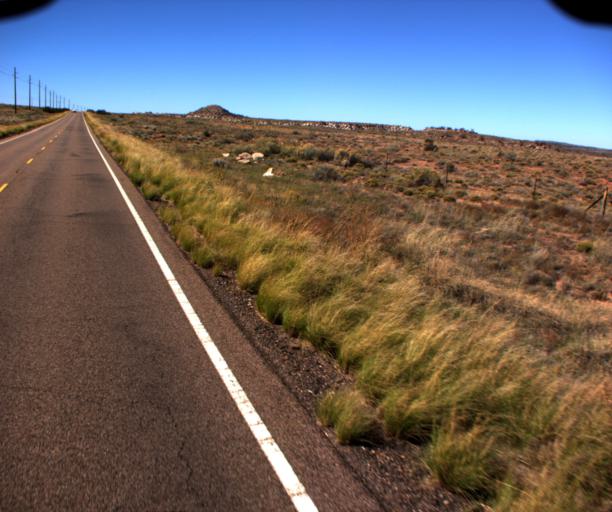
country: US
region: Arizona
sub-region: Navajo County
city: Taylor
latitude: 34.5027
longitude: -110.1914
